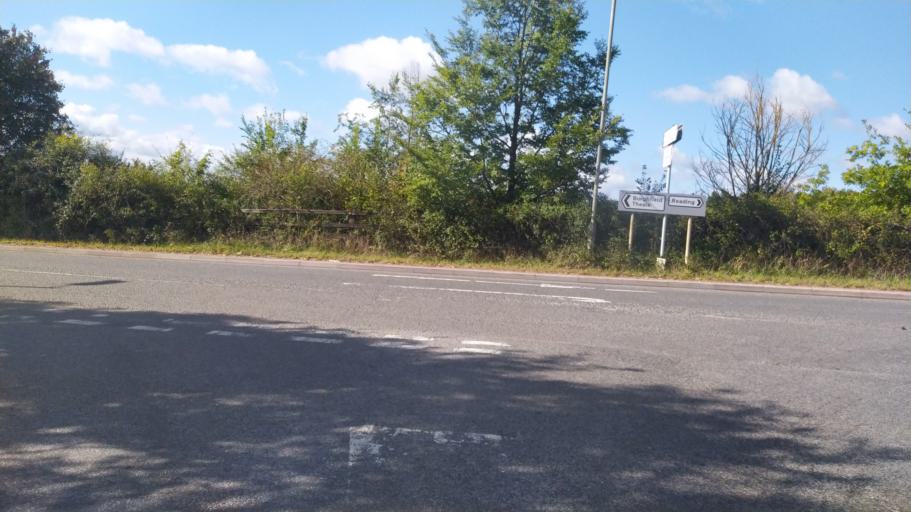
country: GB
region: England
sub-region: West Berkshire
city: Calcot
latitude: 51.4214
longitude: -1.0301
